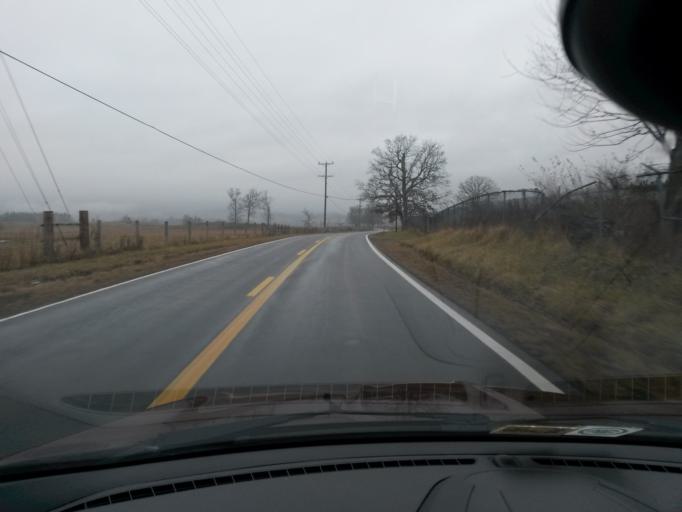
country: US
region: West Virginia
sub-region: Greenbrier County
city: Lewisburg
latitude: 37.8463
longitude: -80.4793
